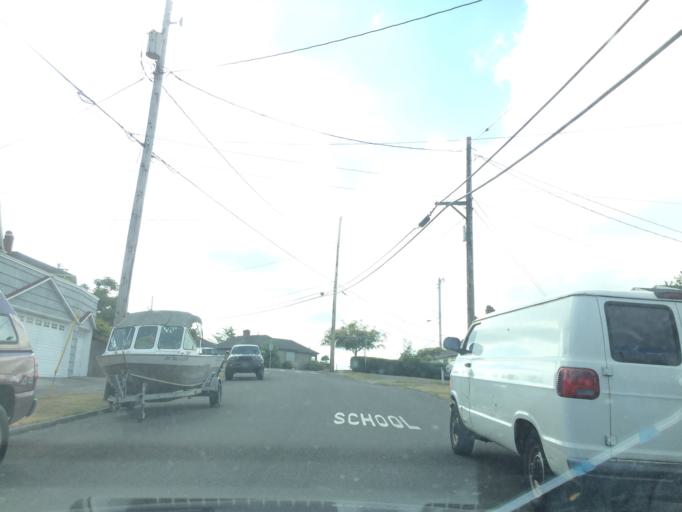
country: US
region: Oregon
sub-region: Clatsop County
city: Astoria
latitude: 46.1817
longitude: -123.8548
